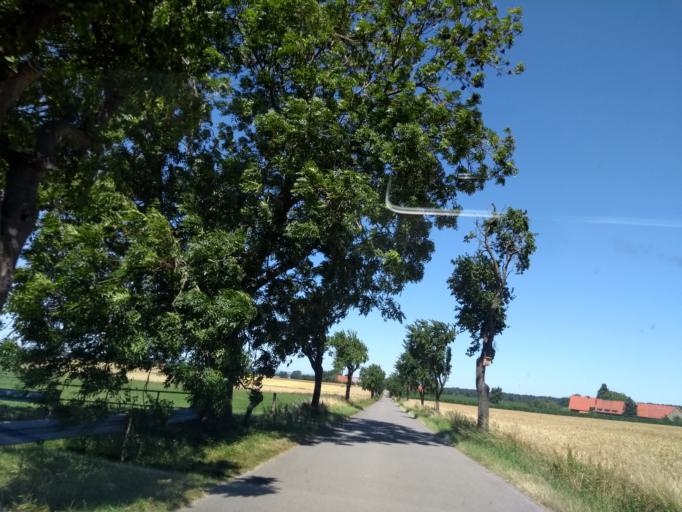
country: DE
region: North Rhine-Westphalia
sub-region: Regierungsbezirk Detmold
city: Salzkotten
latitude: 51.6518
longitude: 8.6381
